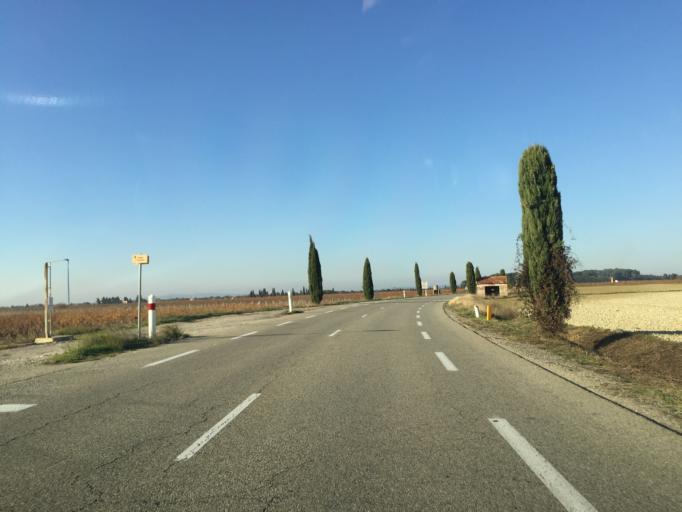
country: FR
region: Provence-Alpes-Cote d'Azur
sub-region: Departement du Vaucluse
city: Sainte-Cecile-les-Vignes
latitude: 44.2331
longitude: 4.9119
